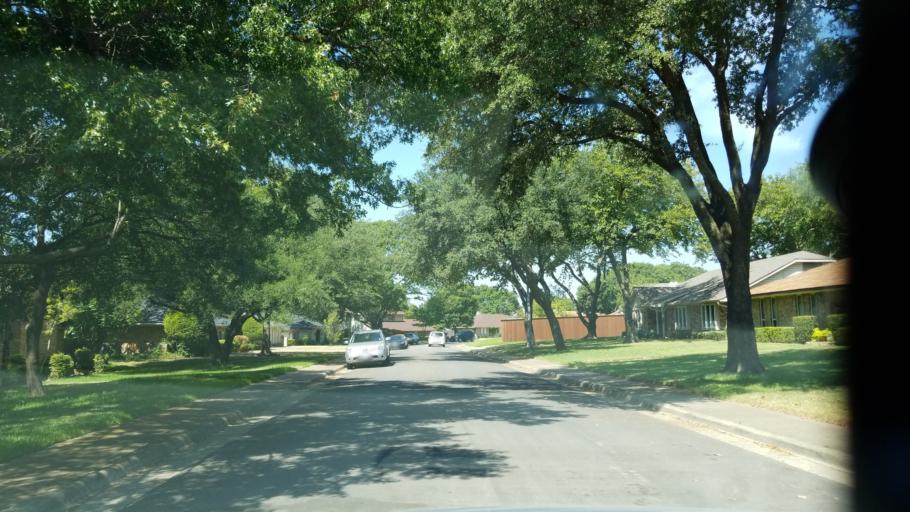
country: US
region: Texas
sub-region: Dallas County
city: Duncanville
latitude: 32.6497
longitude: -96.8952
